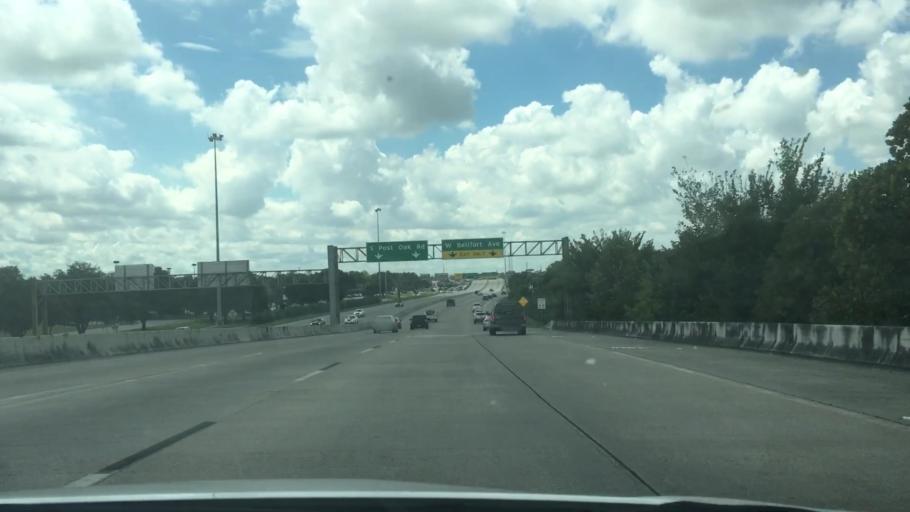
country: US
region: Texas
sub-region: Harris County
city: Bellaire
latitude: 29.6764
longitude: -95.4597
